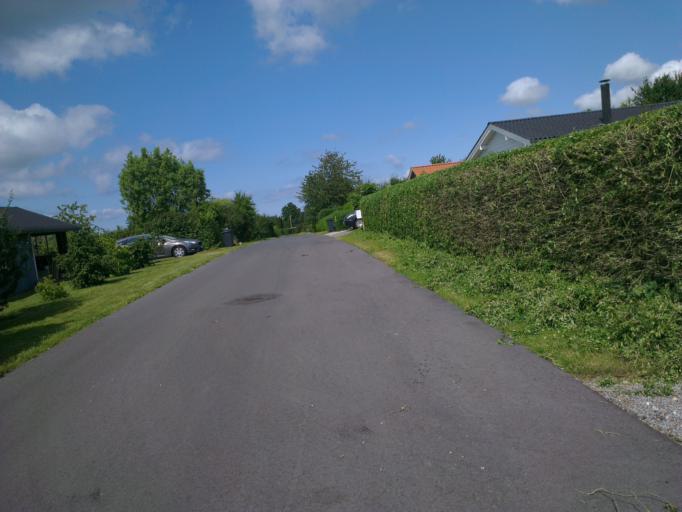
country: DK
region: Zealand
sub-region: Lejre Kommune
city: Ejby
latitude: 55.7455
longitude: 11.8704
